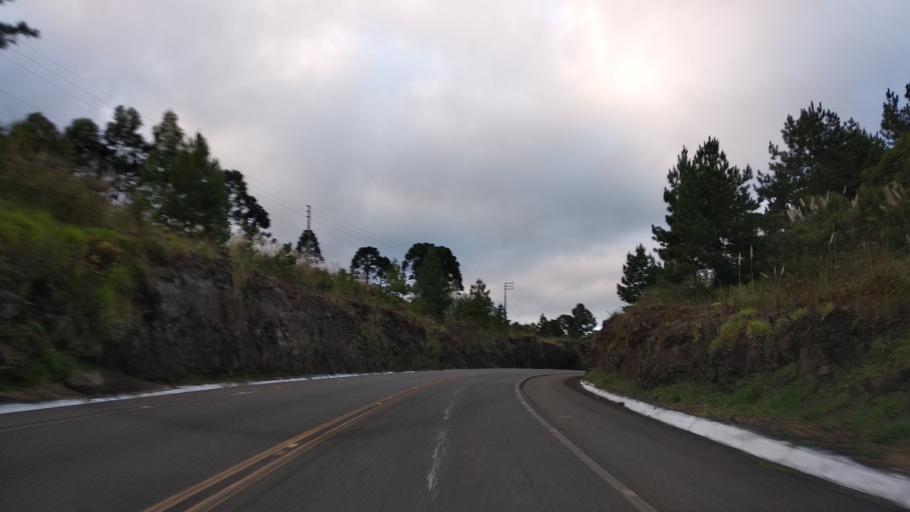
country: BR
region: Santa Catarina
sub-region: Campos Novos
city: Campos Novos
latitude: -27.5005
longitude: -50.9290
